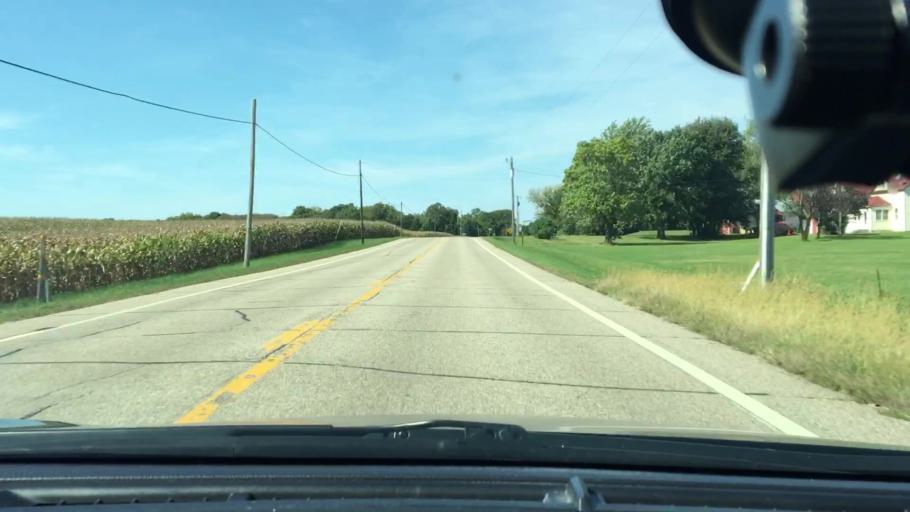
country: US
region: Minnesota
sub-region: Hennepin County
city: Corcoran
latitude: 45.1132
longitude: -93.5799
